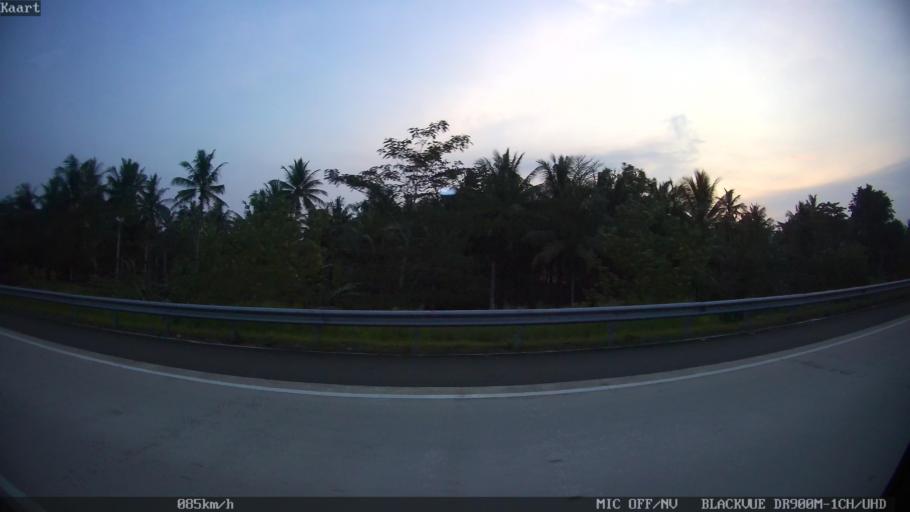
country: ID
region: Lampung
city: Kalianda
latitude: -5.6715
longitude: 105.6017
